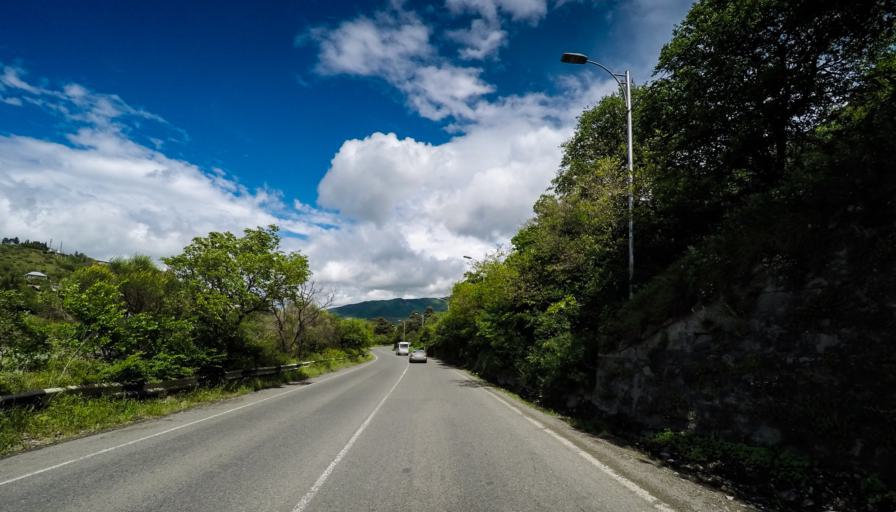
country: GE
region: Mtskheta-Mtianeti
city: Mtskheta
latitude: 41.8381
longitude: 44.7135
